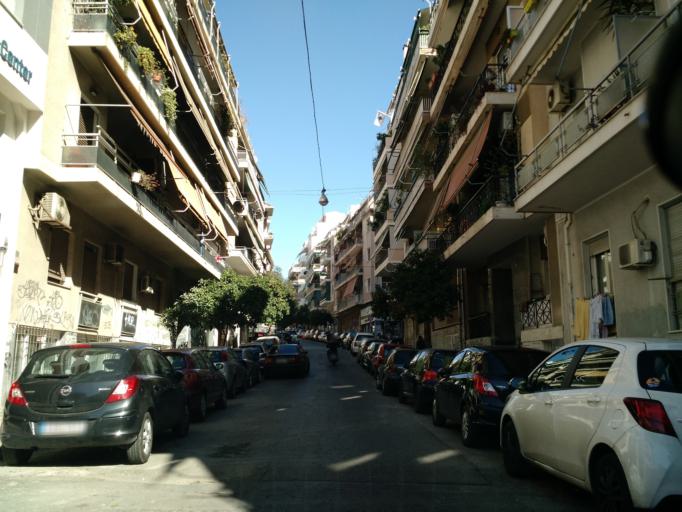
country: GR
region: Attica
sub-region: Nomarchia Athinas
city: Psychiko
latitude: 37.9896
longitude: 23.7623
